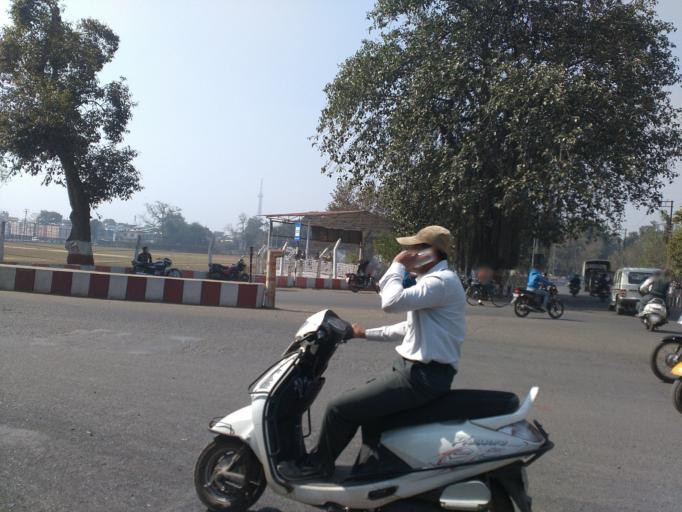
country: IN
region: Madhya Pradesh
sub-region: Jabalpur
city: Jabalpur
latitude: 23.1565
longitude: 79.9512
